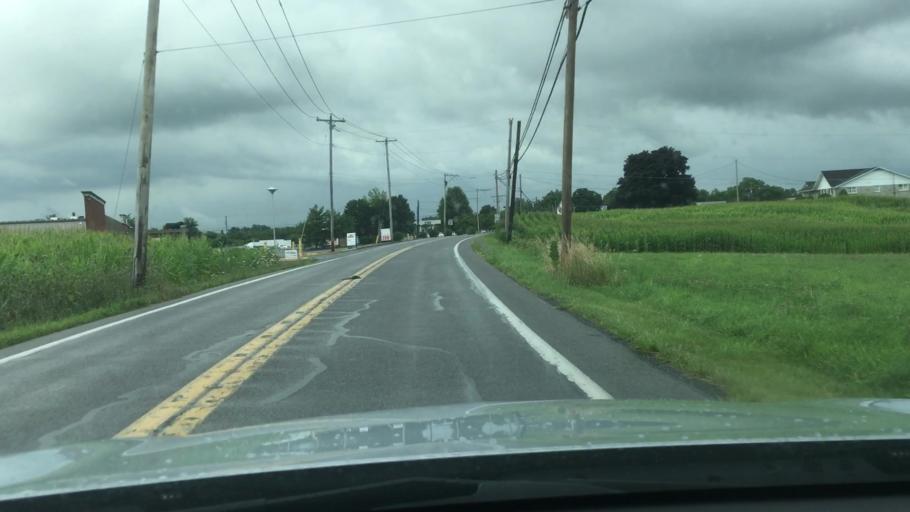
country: US
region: Pennsylvania
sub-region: Franklin County
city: Chambersburg
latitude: 39.9317
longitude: -77.6961
